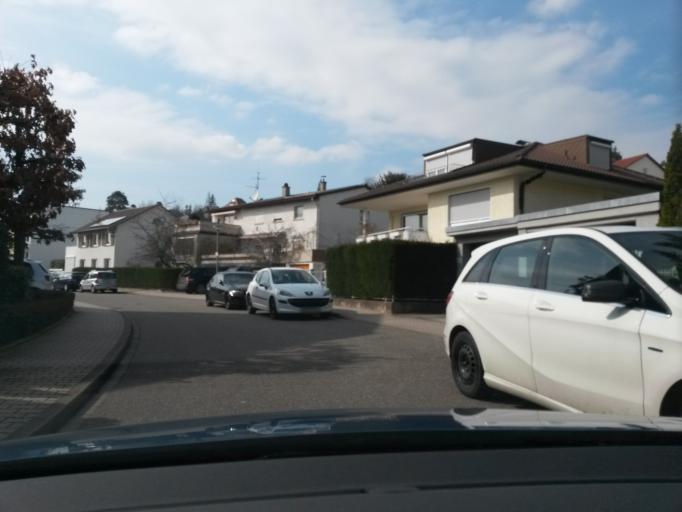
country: DE
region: Baden-Wuerttemberg
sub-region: Karlsruhe Region
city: Pforzheim
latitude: 48.9002
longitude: 8.7129
